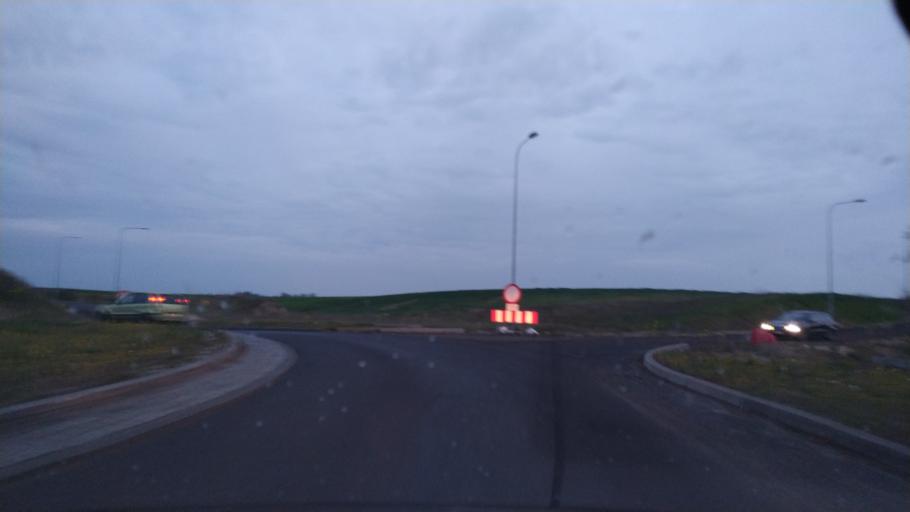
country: PL
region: Greater Poland Voivodeship
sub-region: Powiat pilski
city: Szydlowo
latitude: 53.2450
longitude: 16.6020
